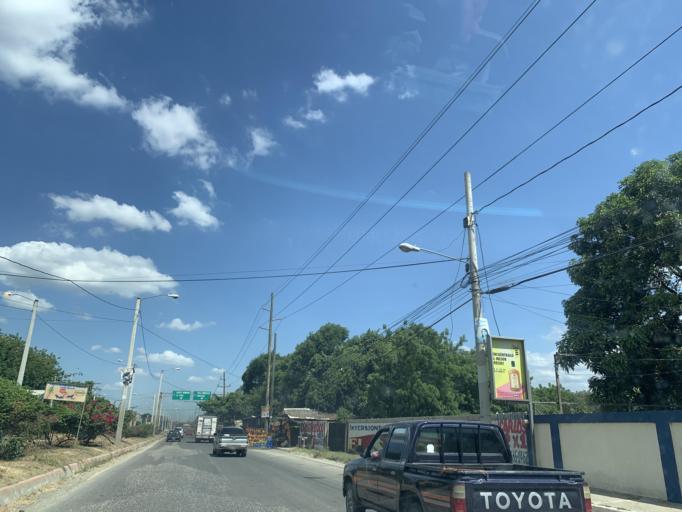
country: DO
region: Santiago
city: Villa Bisono
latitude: 19.5542
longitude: -70.8601
